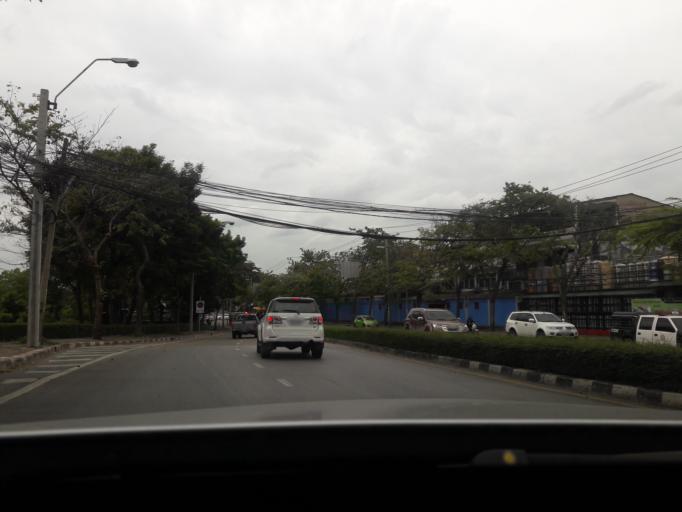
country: TH
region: Bangkok
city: Dusit
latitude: 13.7760
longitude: 100.5284
